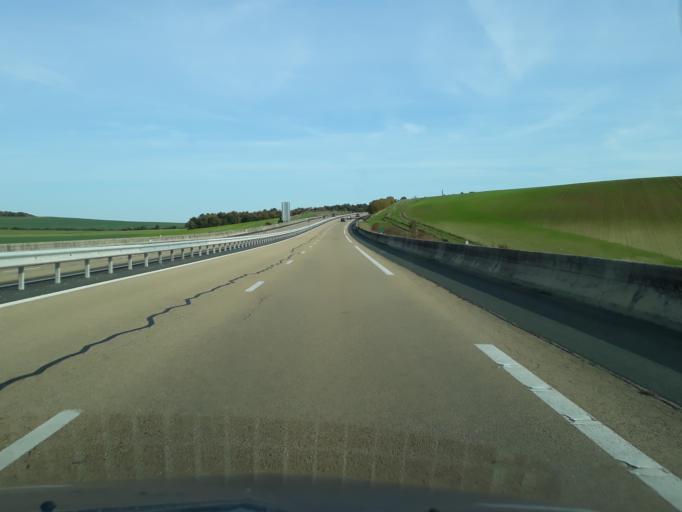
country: FR
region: Champagne-Ardenne
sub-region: Departement de l'Aube
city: Aix-en-Othe
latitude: 48.2627
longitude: 3.6797
